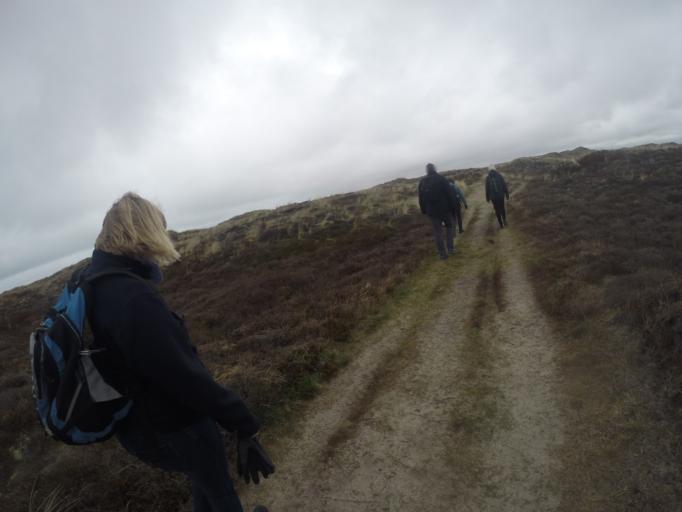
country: DK
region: Central Jutland
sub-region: Lemvig Kommune
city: Thyboron
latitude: 56.8299
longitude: 8.2665
